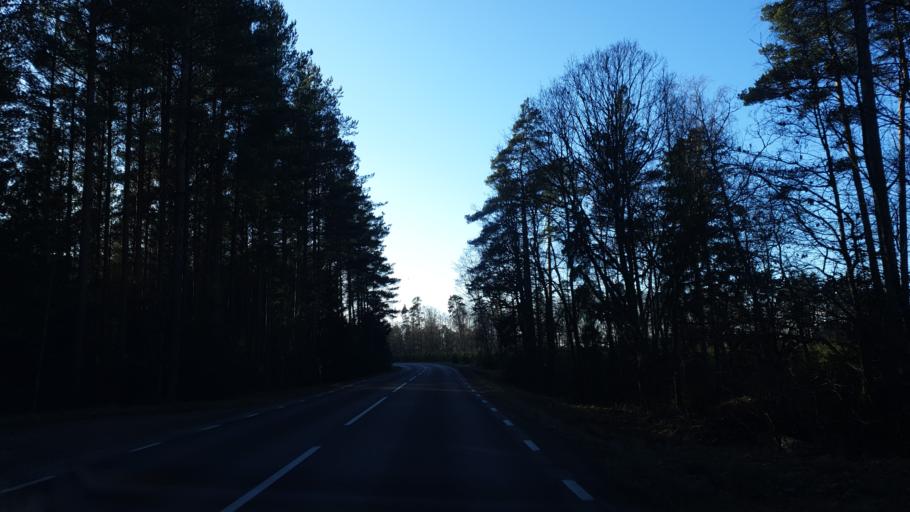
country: SE
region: Blekinge
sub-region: Ronneby Kommun
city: Kallinge
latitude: 56.2081
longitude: 15.3837
